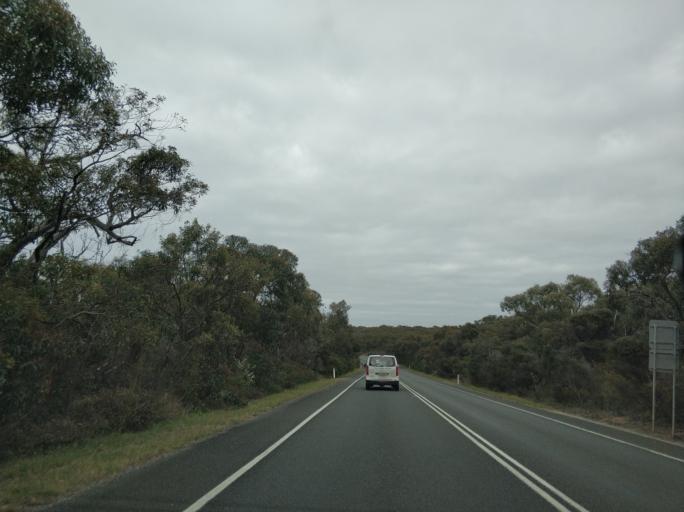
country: AU
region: Victoria
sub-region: Surf Coast
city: Anglesea
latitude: -38.4405
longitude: 144.1213
